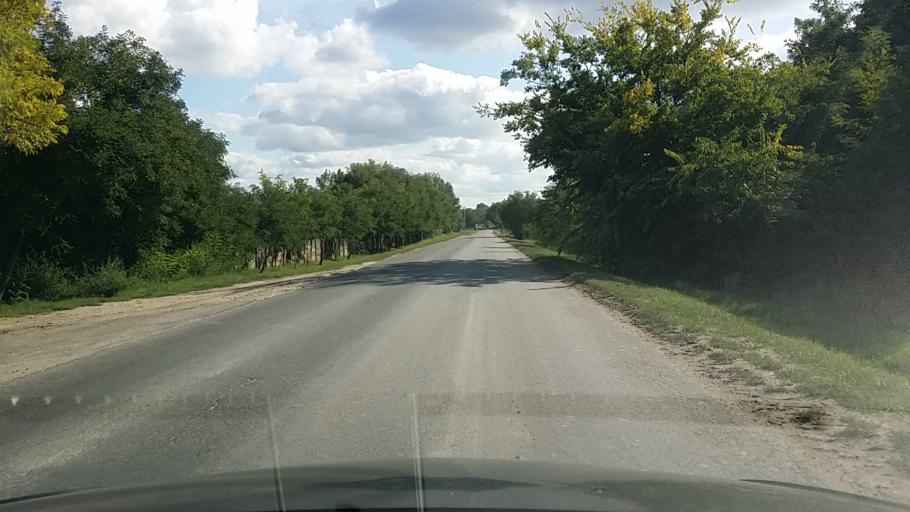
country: HU
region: Pest
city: Taksony
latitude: 47.3141
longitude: 19.0782
